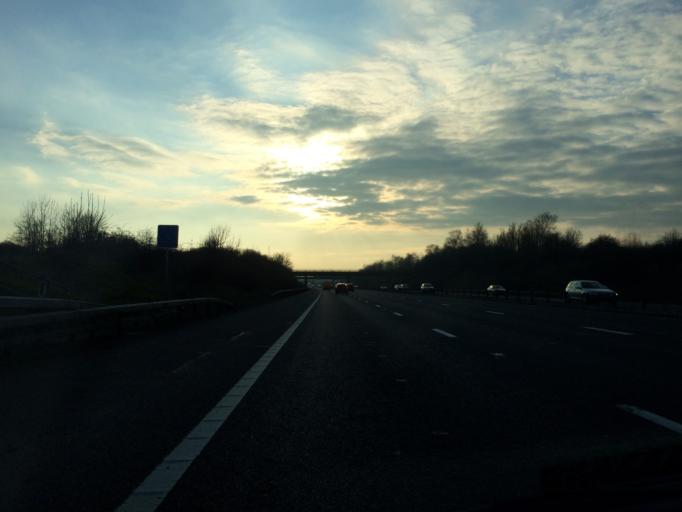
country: GB
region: England
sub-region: Wiltshire
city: Chippenham
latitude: 51.5150
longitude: -2.1167
